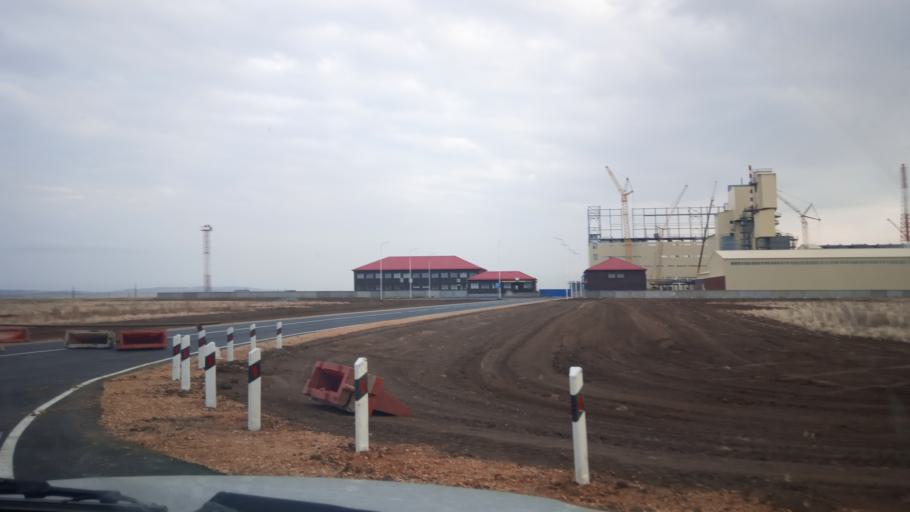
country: RU
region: Orenburg
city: Novotroitsk
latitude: 51.2405
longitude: 58.3267
